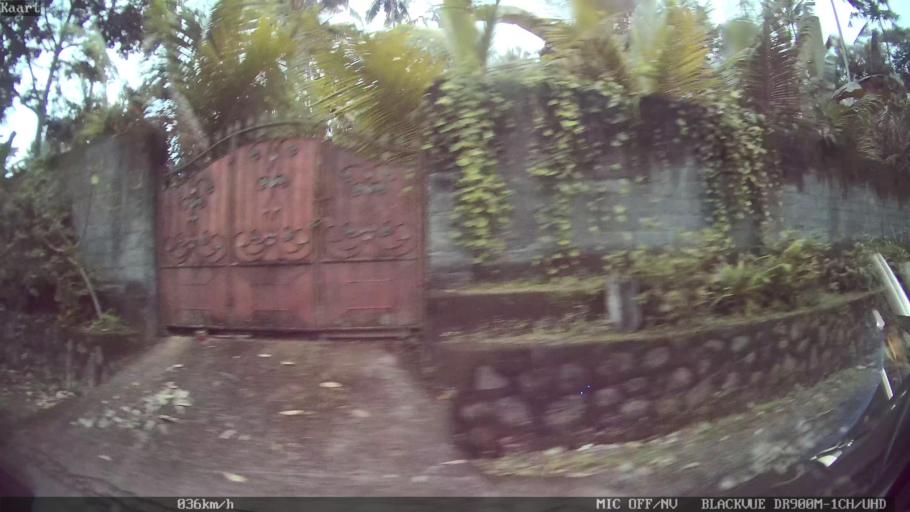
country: ID
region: Bali
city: Banjar Wangsian
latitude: -8.4540
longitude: 115.4187
